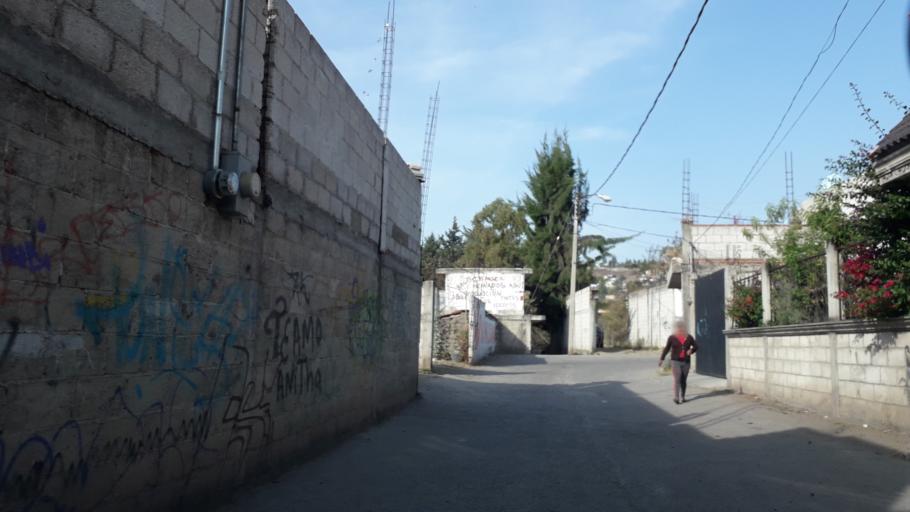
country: MX
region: Puebla
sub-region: Puebla
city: San Andres Azumiatla
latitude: 18.9022
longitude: -98.2527
